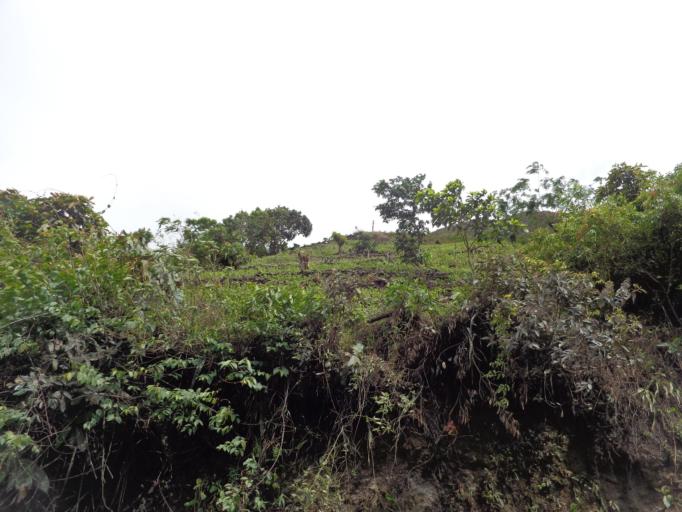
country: BO
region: La Paz
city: Coripata
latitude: -16.3965
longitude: -67.6315
